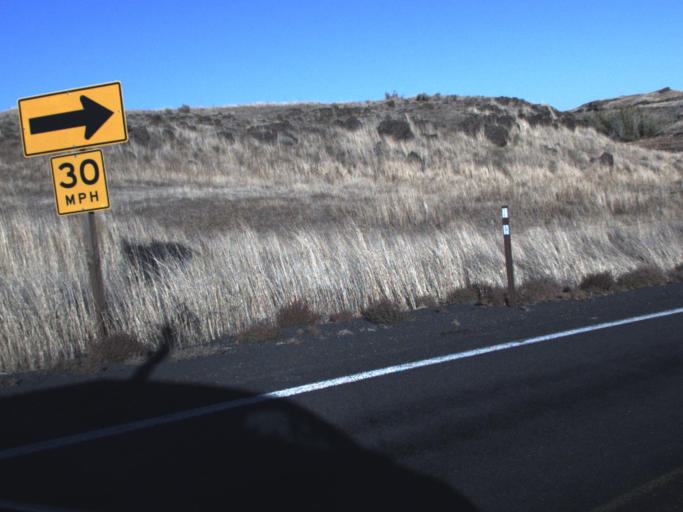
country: US
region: Washington
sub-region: Walla Walla County
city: Waitsburg
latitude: 46.6752
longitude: -118.3249
